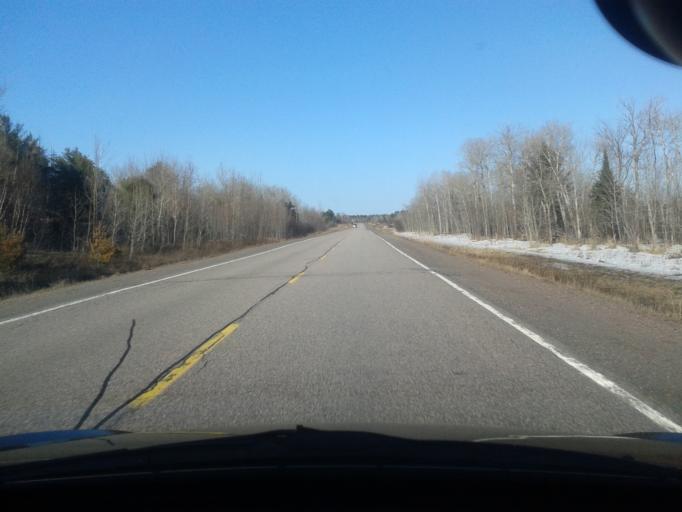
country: CA
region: Ontario
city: Greater Sudbury
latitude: 46.2746
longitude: -80.2841
